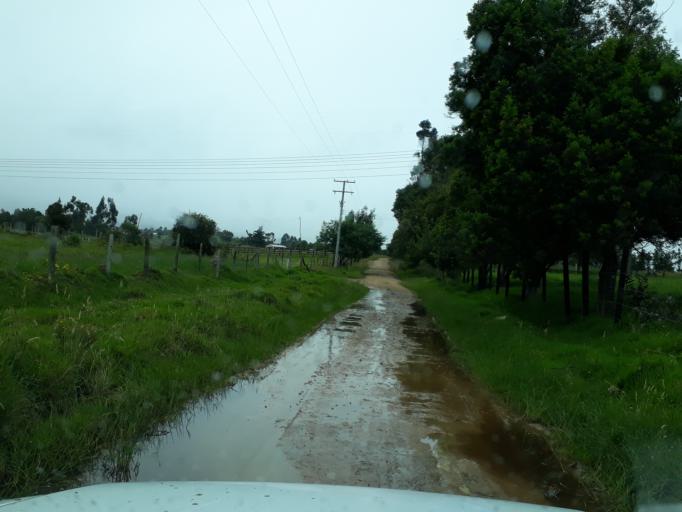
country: CO
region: Cundinamarca
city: Guasca
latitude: 4.8857
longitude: -73.8756
